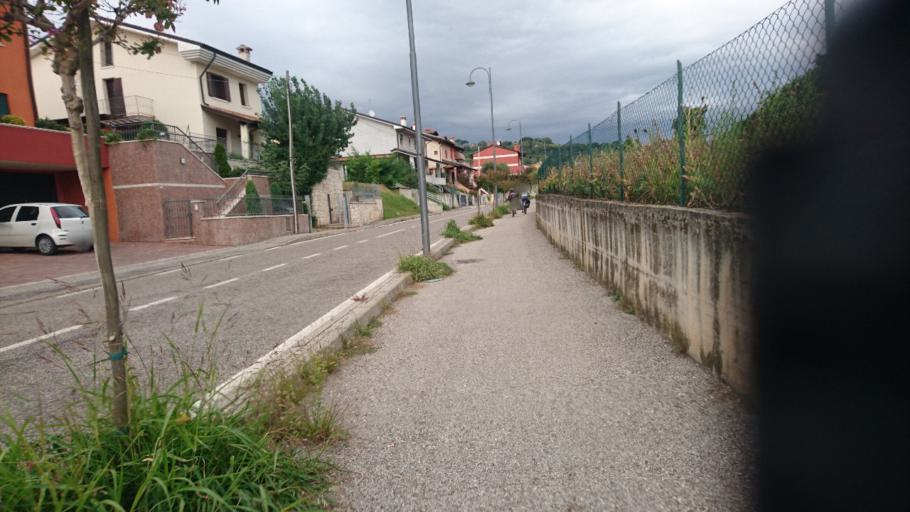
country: IT
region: Veneto
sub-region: Provincia di Vicenza
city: Montebello Vicentino
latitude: 45.4546
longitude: 11.3758
